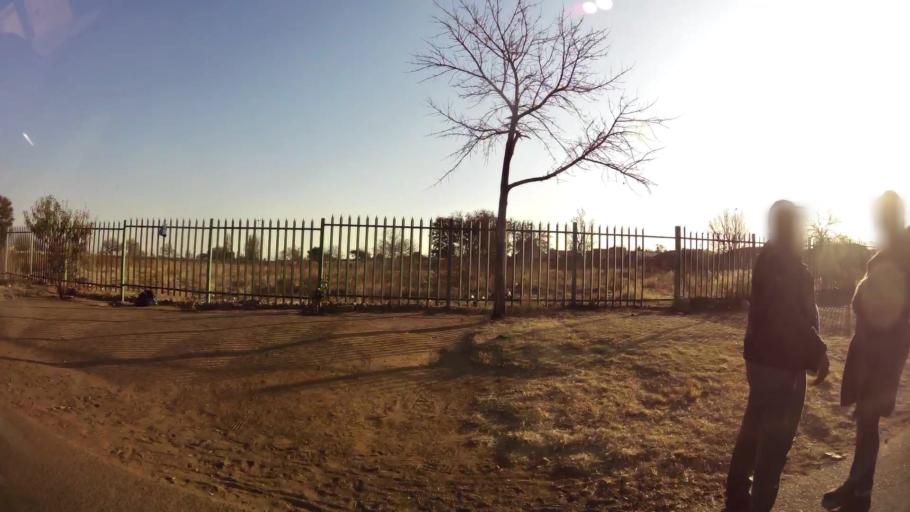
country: ZA
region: Gauteng
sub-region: City of Johannesburg Metropolitan Municipality
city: Soweto
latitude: -26.2531
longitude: 27.8842
